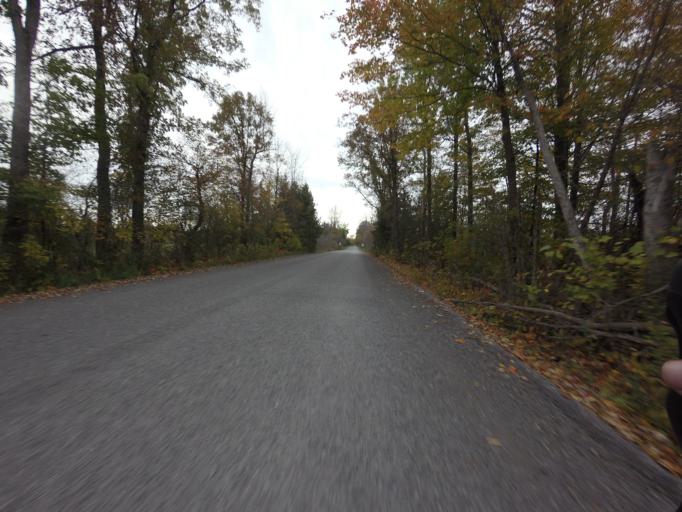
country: CA
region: Ontario
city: Bells Corners
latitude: 45.0738
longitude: -75.7570
